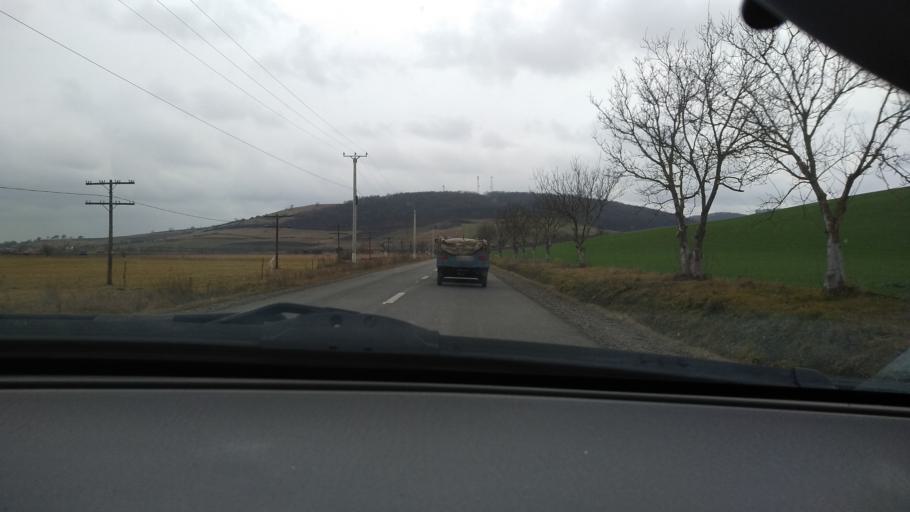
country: RO
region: Mures
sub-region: Comuna Miercurea Nirajului
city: Miercurea Nirajului
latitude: 46.5300
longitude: 24.7789
